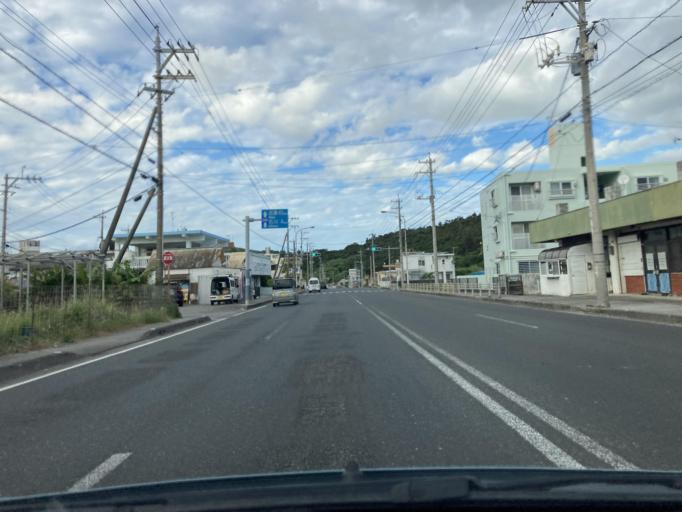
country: JP
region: Okinawa
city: Ishikawa
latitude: 26.3928
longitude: 127.8325
